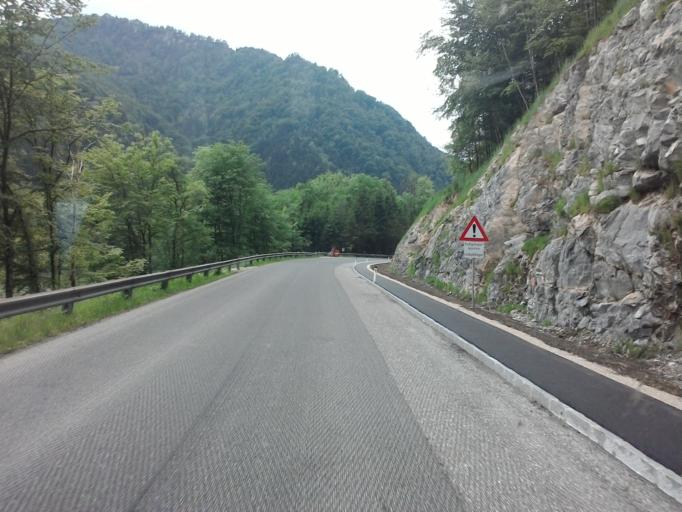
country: AT
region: Upper Austria
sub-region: Politischer Bezirk Steyr-Land
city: Maria Neustift
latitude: 47.8857
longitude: 14.5350
